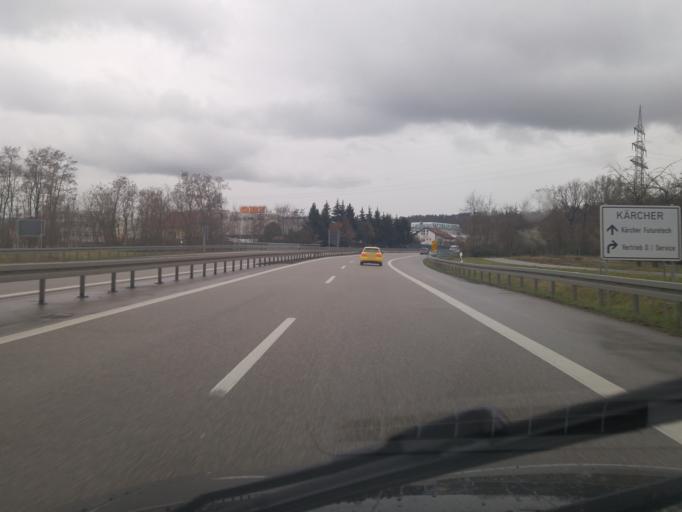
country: DE
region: Baden-Wuerttemberg
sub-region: Regierungsbezirk Stuttgart
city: Leutenbach
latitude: 48.8761
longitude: 9.3817
